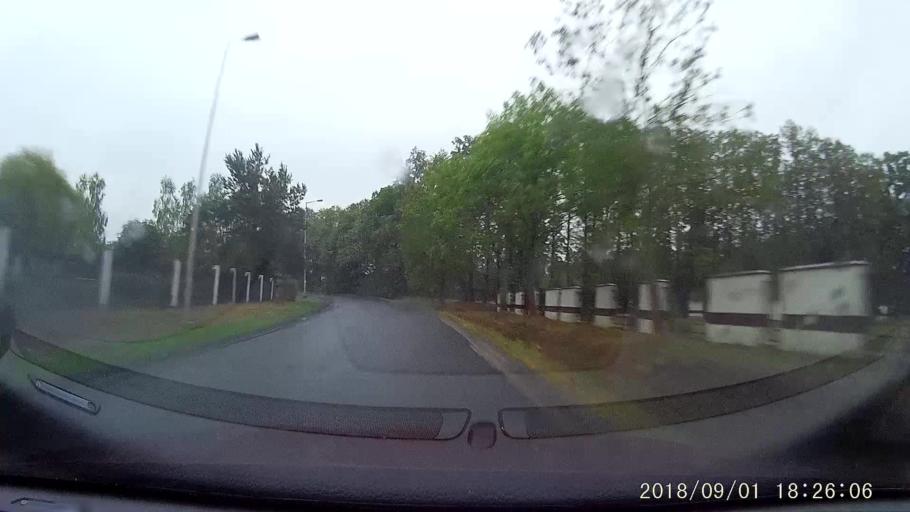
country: PL
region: Lower Silesian Voivodeship
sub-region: Powiat zgorzelecki
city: Piensk
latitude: 51.2279
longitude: 15.0324
